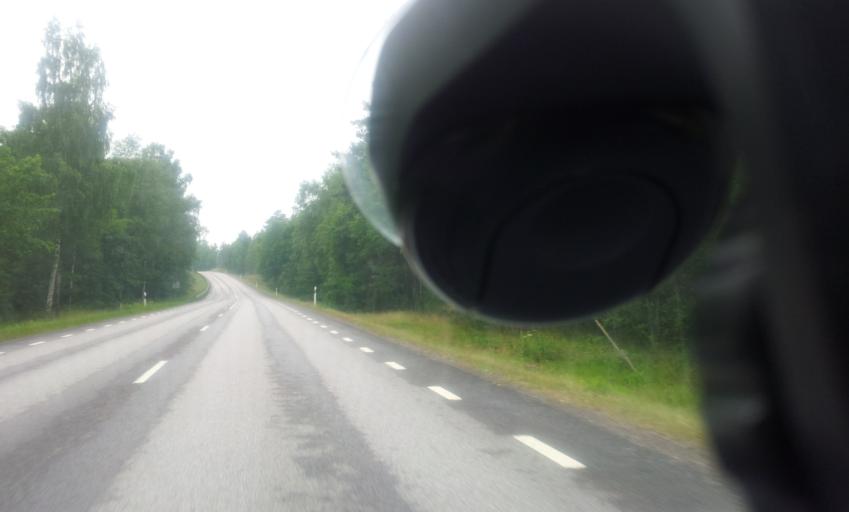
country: SE
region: Kalmar
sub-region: Vasterviks Kommun
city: Ankarsrum
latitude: 57.7224
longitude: 16.4749
